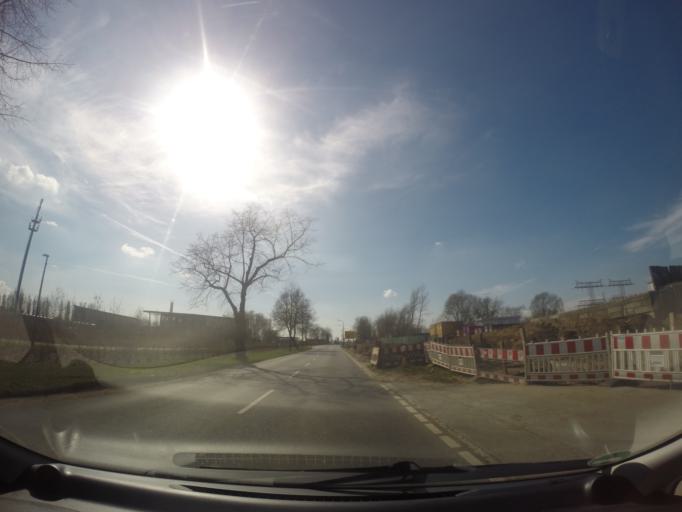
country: DE
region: Berlin
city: Falkenberg
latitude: 52.5581
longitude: 13.5302
